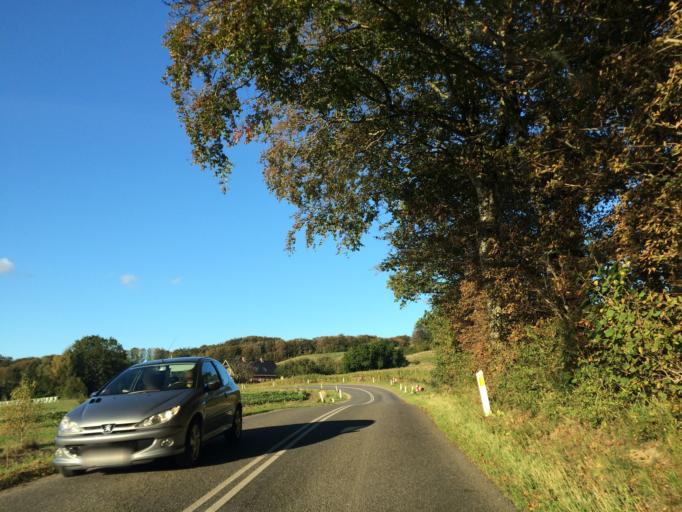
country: DK
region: Central Jutland
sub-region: Skanderborg Kommune
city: Ry
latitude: 56.1200
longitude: 9.7343
